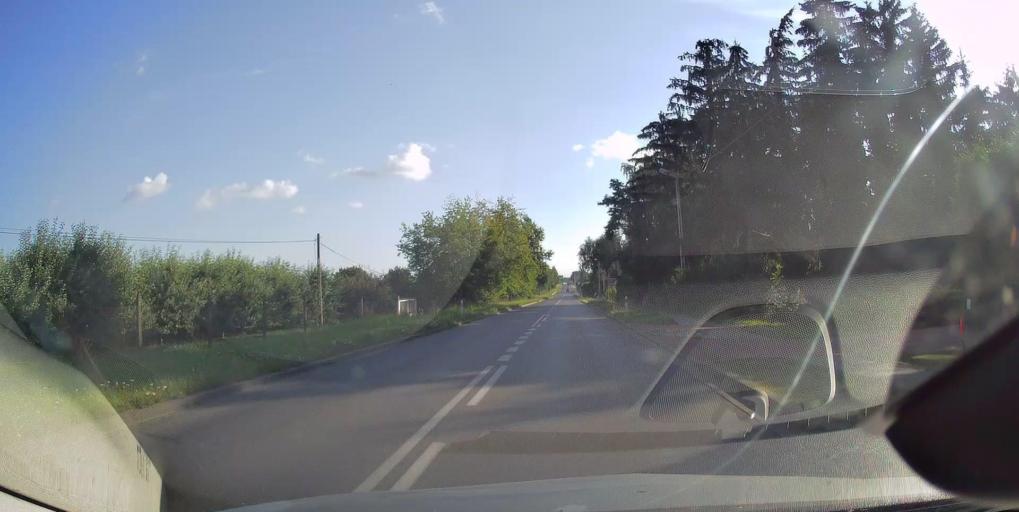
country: PL
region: Masovian Voivodeship
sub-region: Powiat grojecki
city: Belsk Duzy
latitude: 51.8301
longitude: 20.8151
